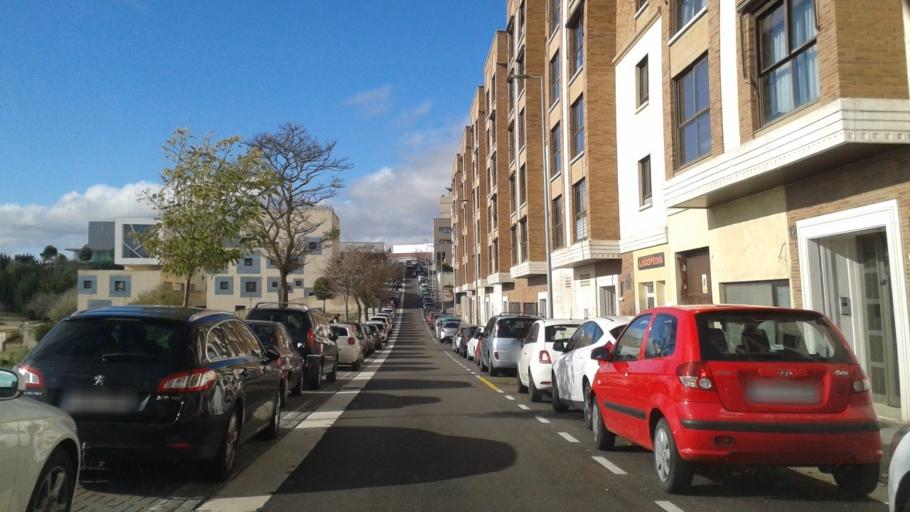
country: ES
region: Castille and Leon
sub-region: Provincia de Valladolid
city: Zaratan
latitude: 41.6355
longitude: -4.7631
